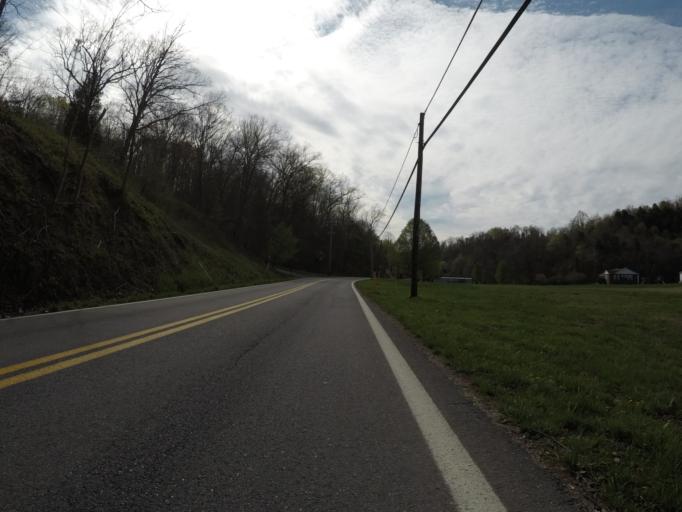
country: US
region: West Virginia
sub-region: Cabell County
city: Pea Ridge
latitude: 38.3805
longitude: -82.3750
